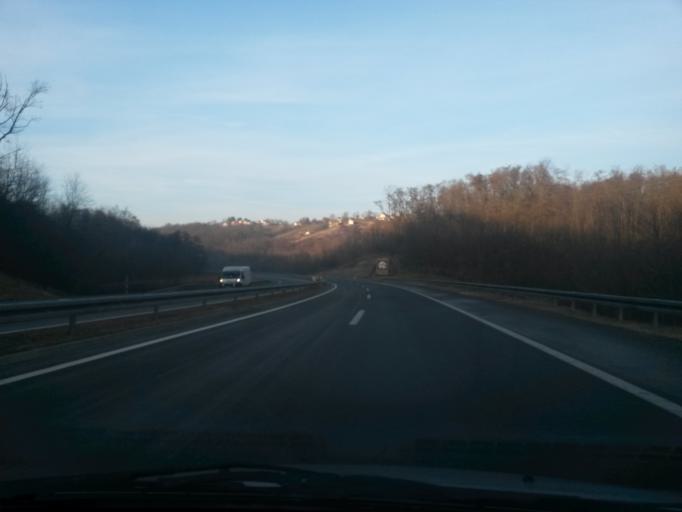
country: HR
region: Varazdinska
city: Jalzabet
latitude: 46.2356
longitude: 16.4103
